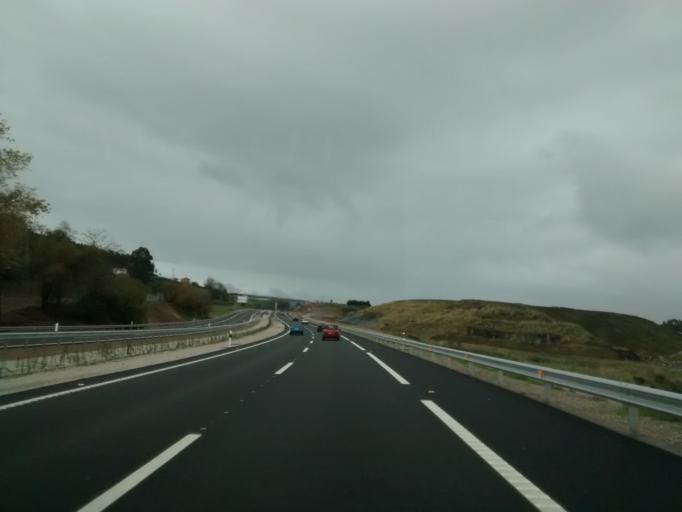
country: ES
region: Cantabria
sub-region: Provincia de Cantabria
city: Polanco
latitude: 43.3461
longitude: -4.0032
